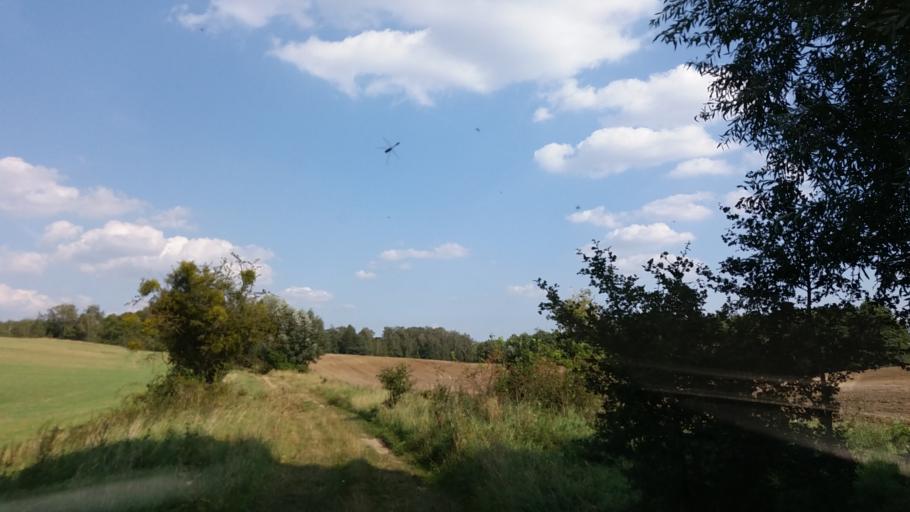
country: PL
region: West Pomeranian Voivodeship
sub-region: Powiat choszczenski
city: Krzecin
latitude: 53.1030
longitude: 15.4323
